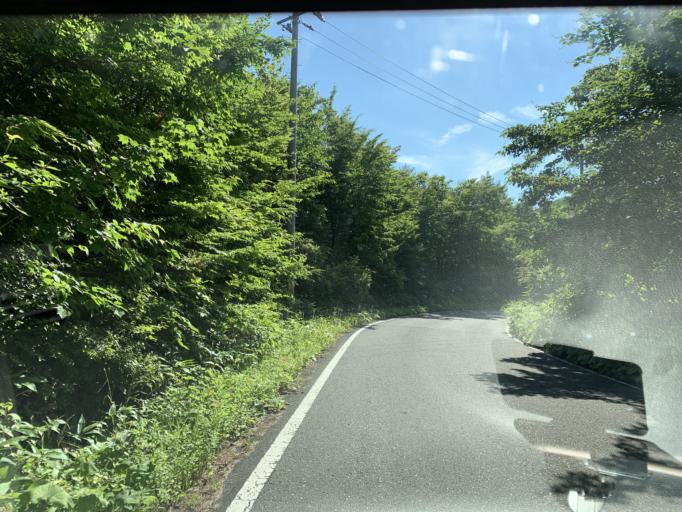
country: JP
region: Iwate
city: Ichinoseki
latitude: 38.8987
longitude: 140.8831
